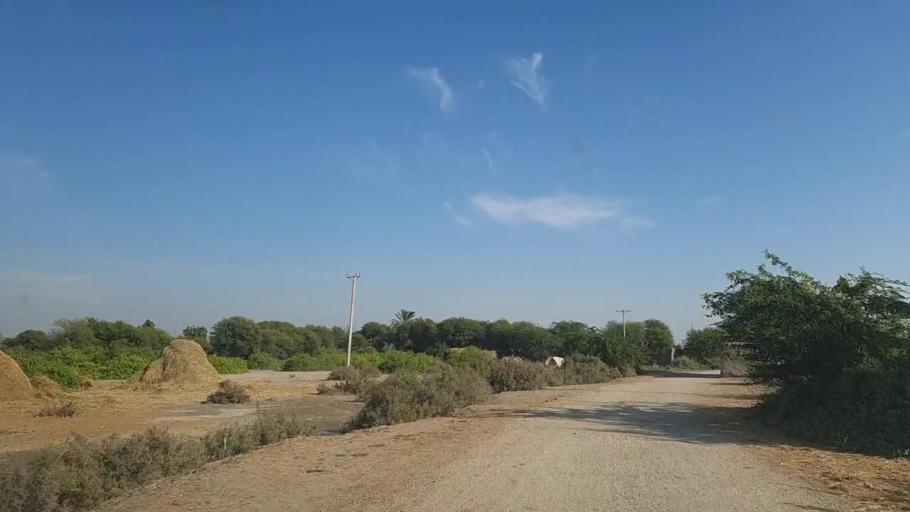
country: PK
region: Sindh
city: Mirpur Batoro
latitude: 24.7666
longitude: 68.3478
